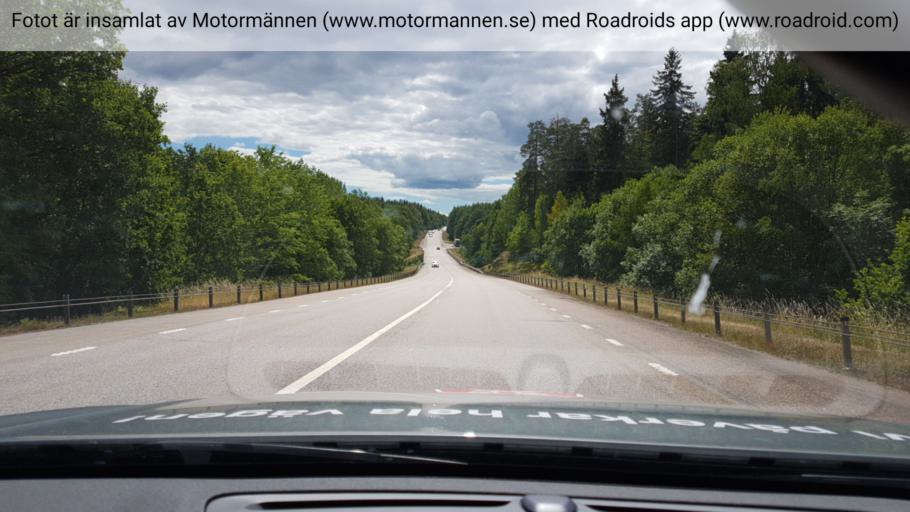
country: SE
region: Kalmar
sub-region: Vasterviks Kommun
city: Ankarsrum
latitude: 57.5527
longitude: 16.4753
